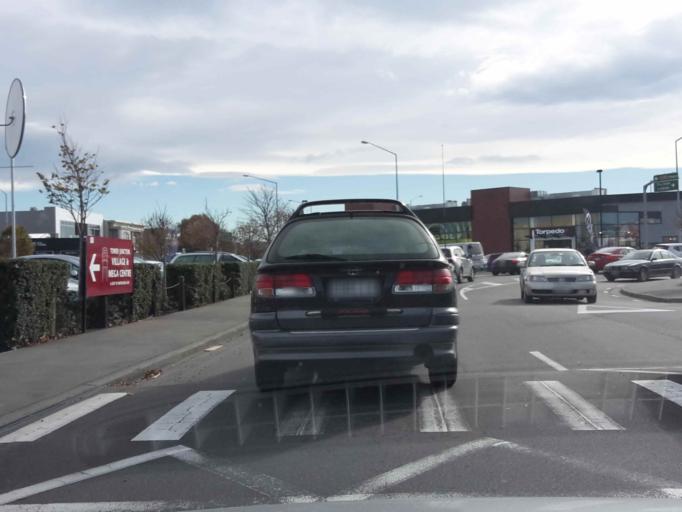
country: NZ
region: Canterbury
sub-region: Christchurch City
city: Christchurch
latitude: -43.5379
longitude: 172.6067
